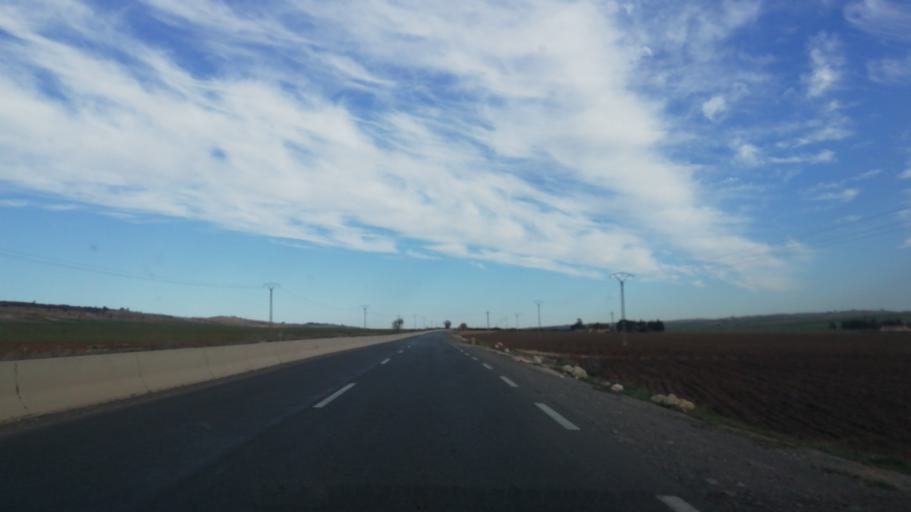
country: DZ
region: Sidi Bel Abbes
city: Sfizef
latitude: 35.1807
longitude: -0.4124
